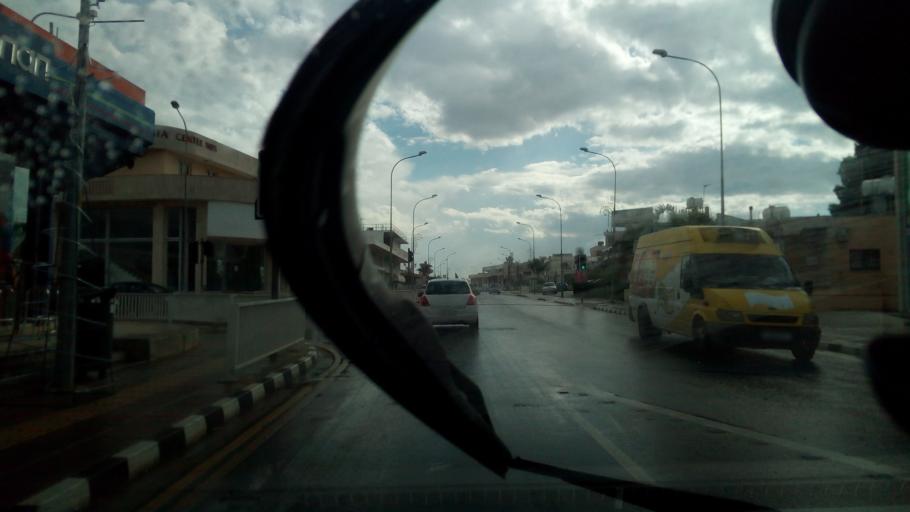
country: CY
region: Ammochostos
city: Deryneia
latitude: 35.0598
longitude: 33.9659
